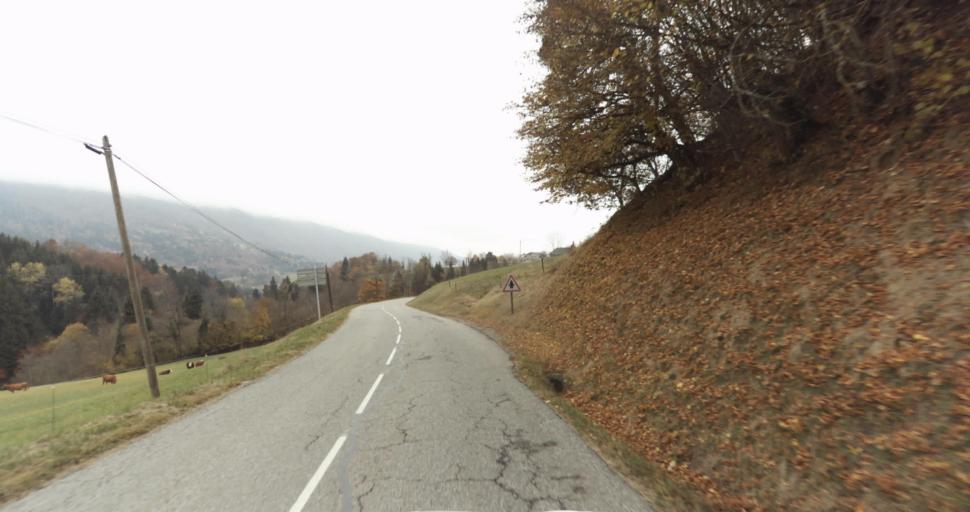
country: FR
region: Rhone-Alpes
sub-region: Departement de la Haute-Savoie
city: Saint-Jorioz
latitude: 45.7982
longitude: 6.1517
